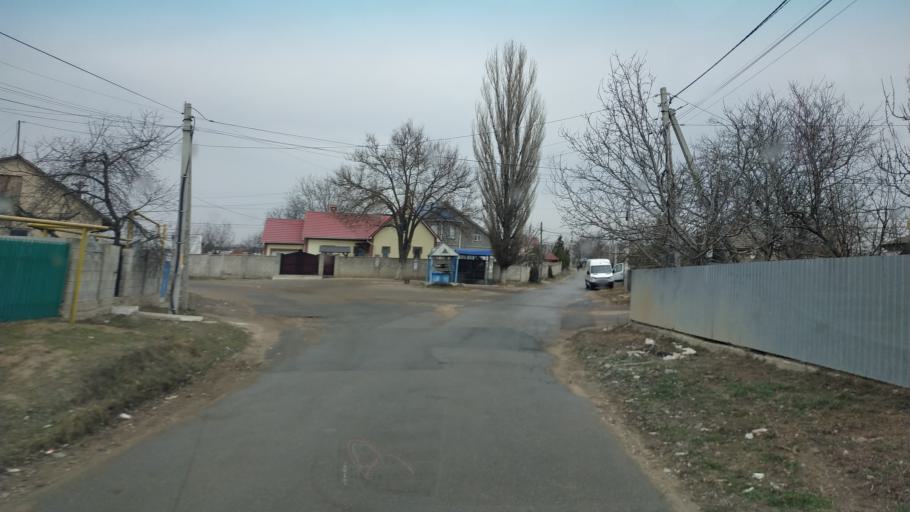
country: MD
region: Chisinau
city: Singera
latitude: 46.9084
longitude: 28.9439
